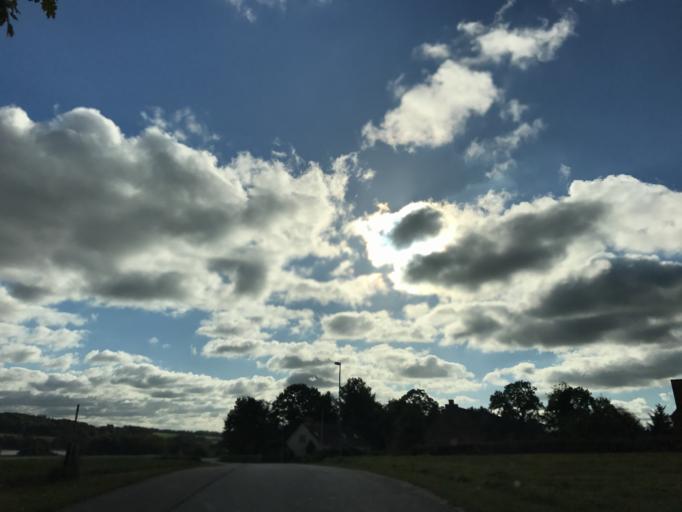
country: DK
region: Central Jutland
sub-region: Silkeborg Kommune
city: Kjellerup
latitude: 56.2629
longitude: 9.5080
